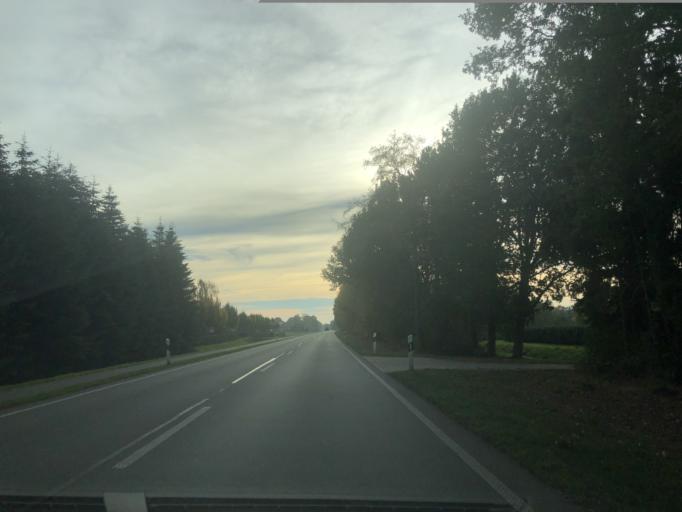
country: DE
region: Lower Saxony
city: Bosel
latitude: 53.0716
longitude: 7.9256
